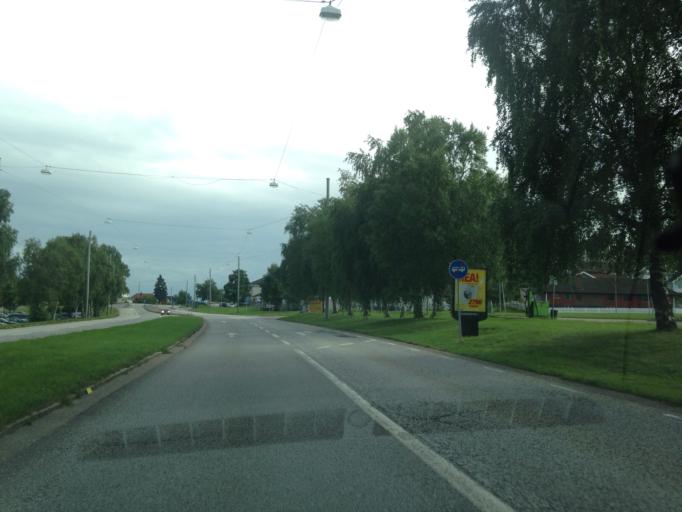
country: SE
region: Vaestra Goetaland
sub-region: Goteborg
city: Goeteborg
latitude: 57.7413
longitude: 11.9736
